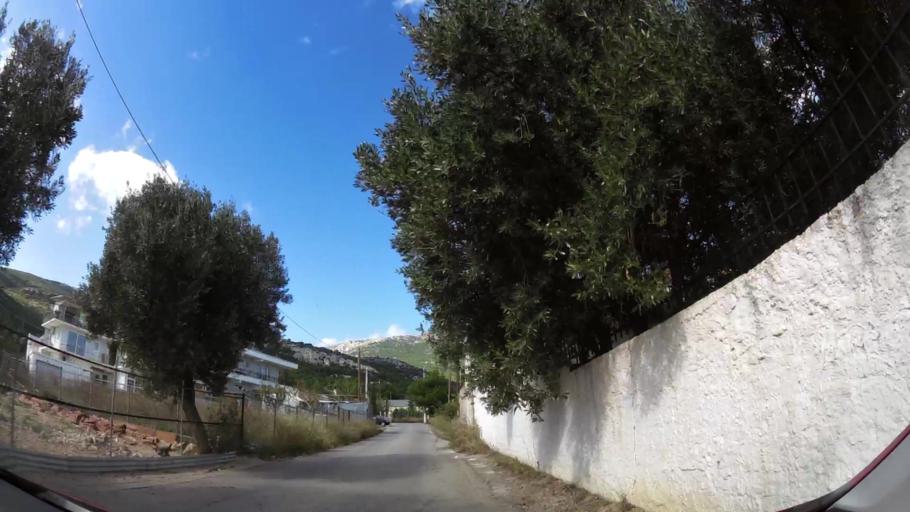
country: GR
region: Attica
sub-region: Nomarchia Anatolikis Attikis
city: Thrakomakedones
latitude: 38.1161
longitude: 23.7302
